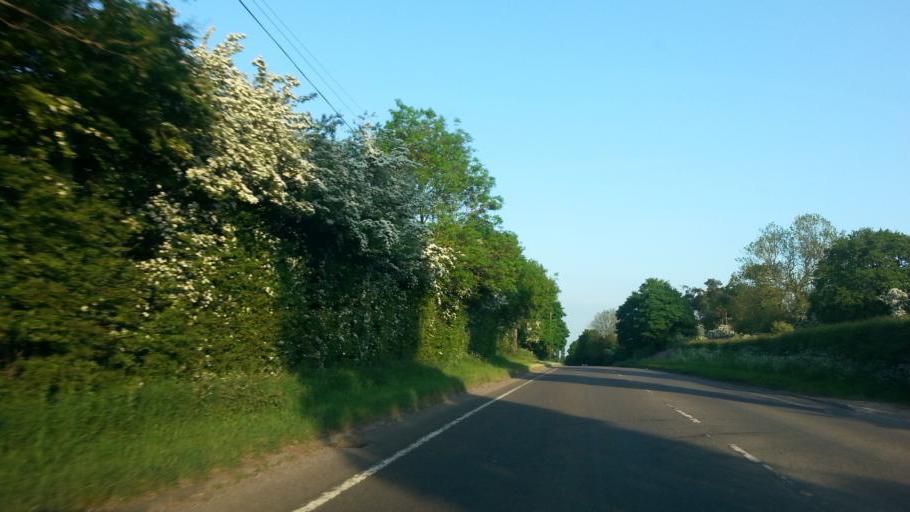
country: GB
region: England
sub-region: Staffordshire
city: Stone
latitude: 52.8733
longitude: -2.0977
